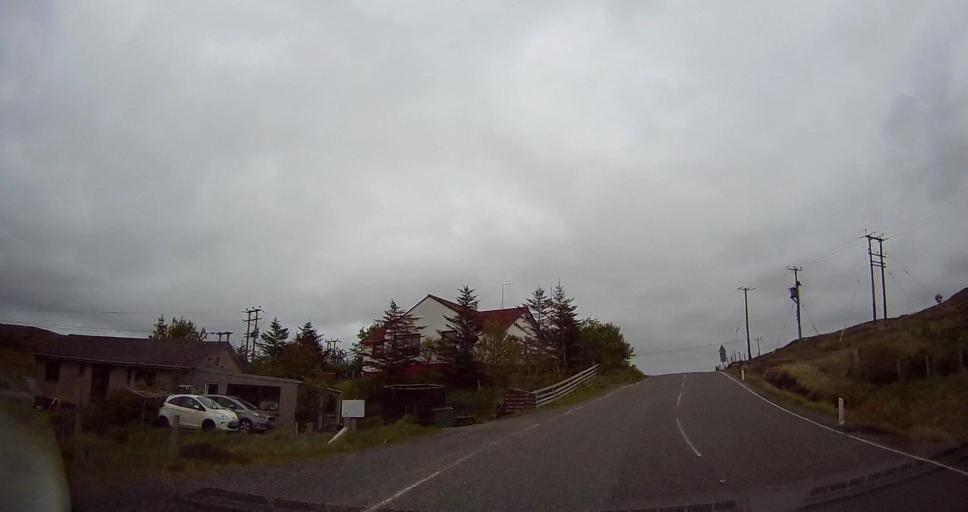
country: GB
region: Scotland
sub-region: Shetland Islands
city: Lerwick
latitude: 60.3497
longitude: -1.2579
